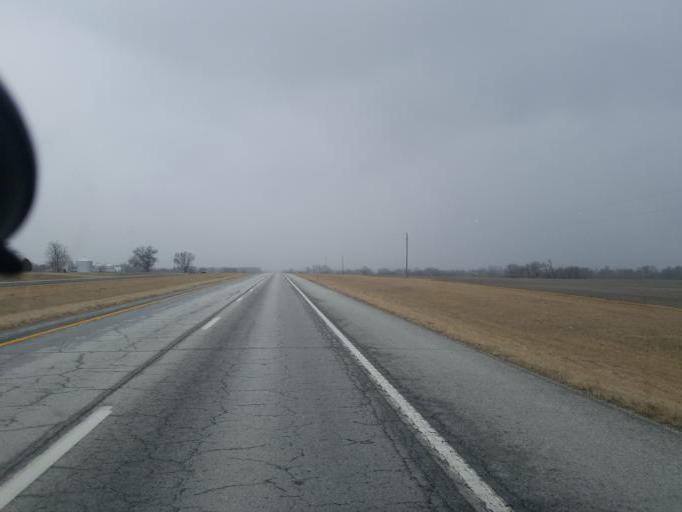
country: US
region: Missouri
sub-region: Macon County
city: La Plata
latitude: 40.0091
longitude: -92.4753
